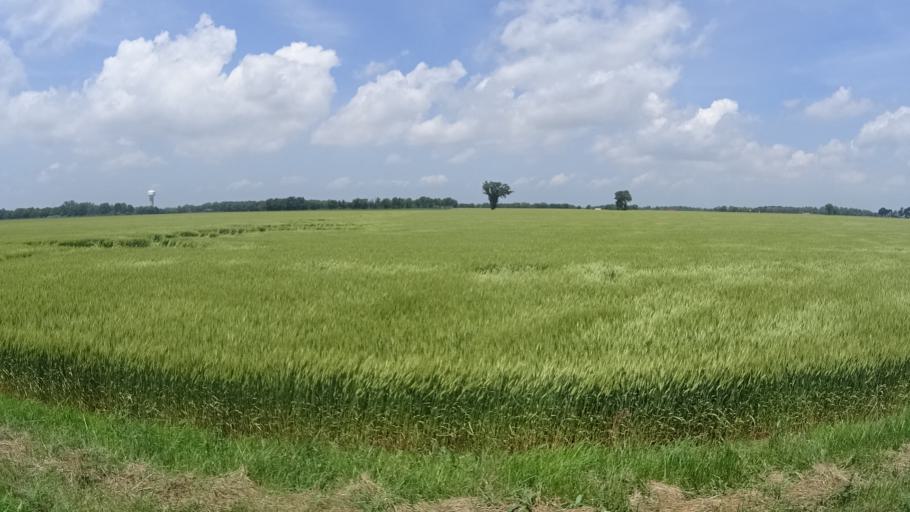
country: US
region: Ohio
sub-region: Huron County
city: Monroeville
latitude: 41.3245
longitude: -82.7534
